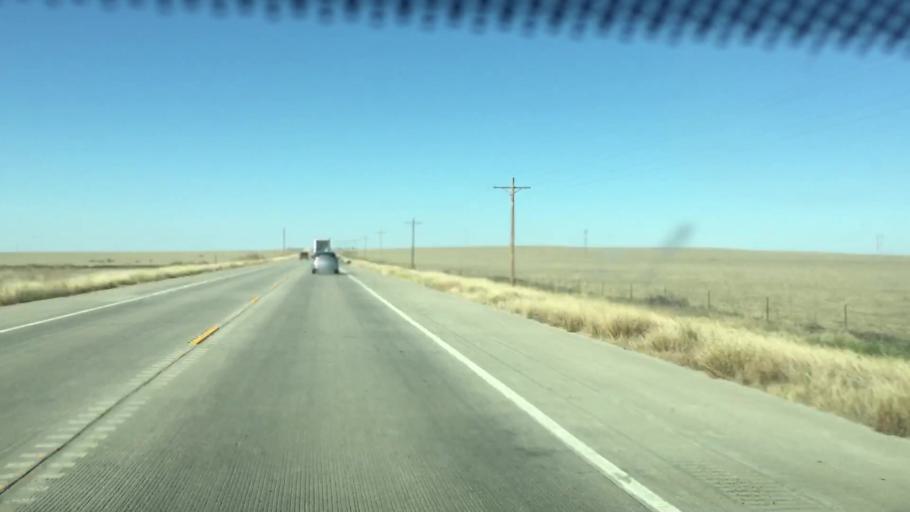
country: US
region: Colorado
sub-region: Prowers County
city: Lamar
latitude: 38.2580
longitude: -102.7239
